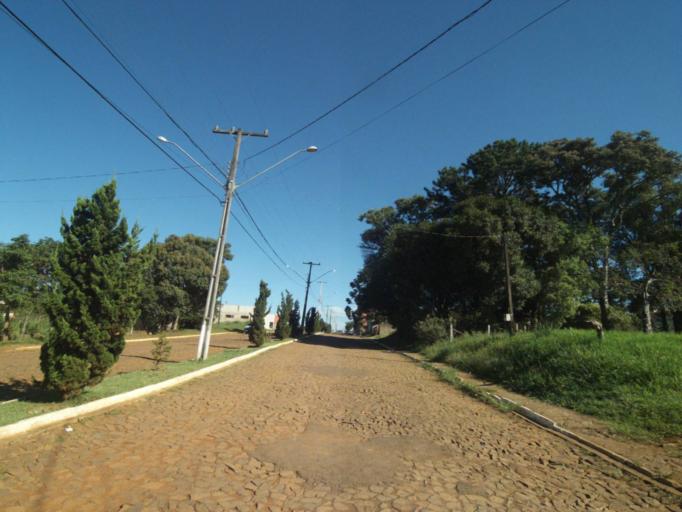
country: BR
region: Parana
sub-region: Pinhao
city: Pinhao
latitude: -25.8374
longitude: -52.0293
